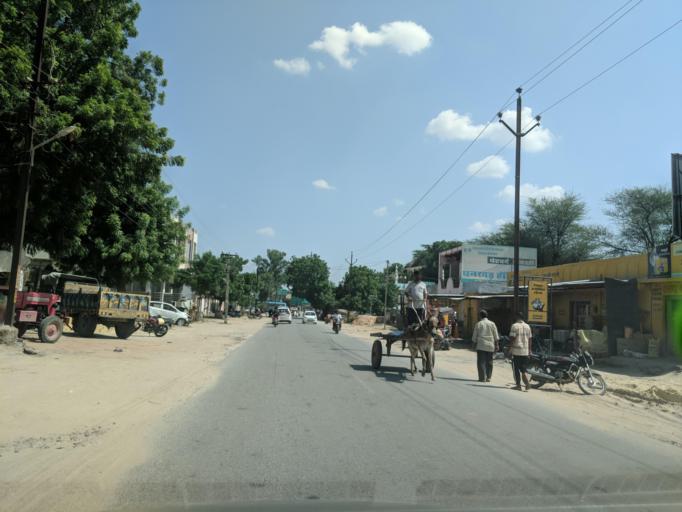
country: IN
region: Rajasthan
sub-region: Jhunjhunun
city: Jhunjhunun
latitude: 28.1352
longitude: 75.3896
